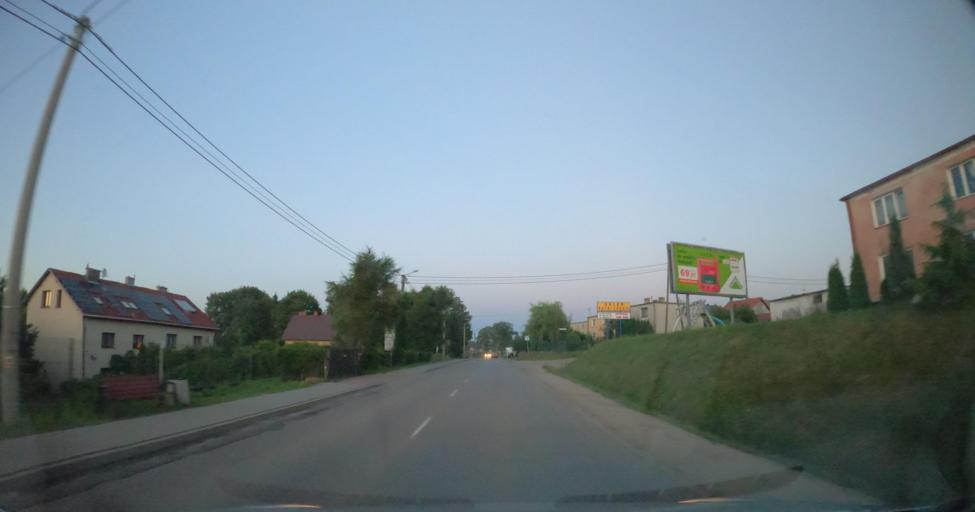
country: PL
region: Pomeranian Voivodeship
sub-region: Powiat wejherowski
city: Szemud
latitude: 54.4862
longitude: 18.2298
